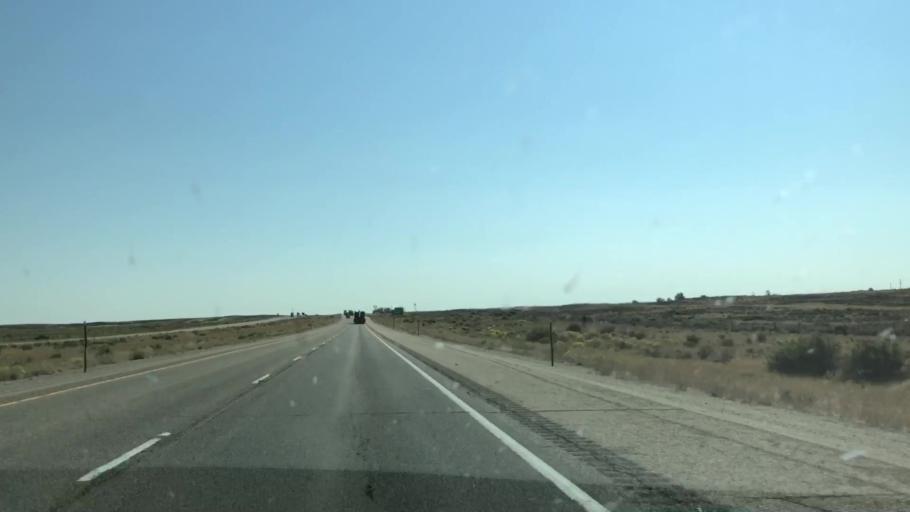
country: US
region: Wyoming
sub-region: Sweetwater County
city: Rock Springs
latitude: 41.6357
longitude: -108.4211
